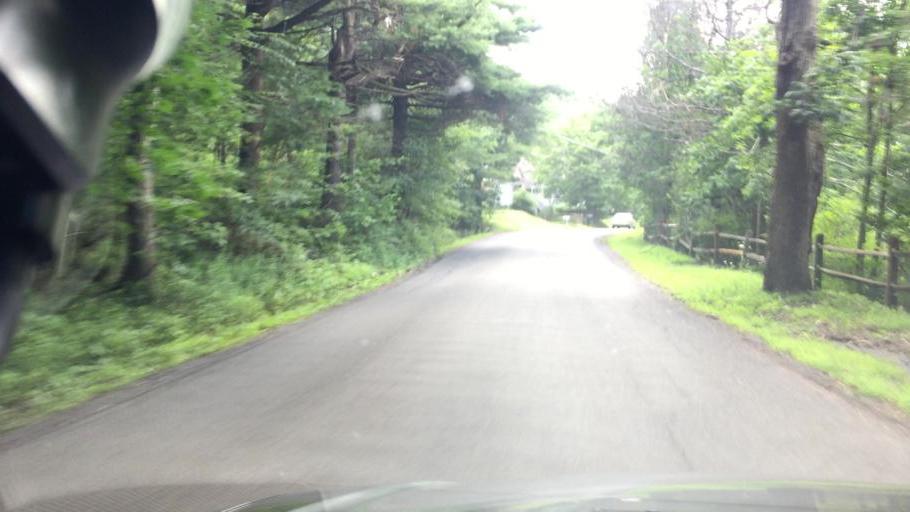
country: US
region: Pennsylvania
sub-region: Luzerne County
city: Oakdale
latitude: 41.0179
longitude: -75.9341
